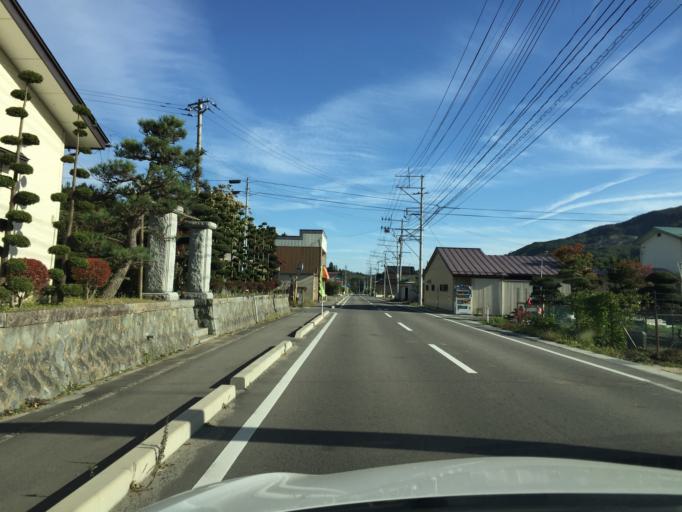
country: JP
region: Fukushima
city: Funehikimachi-funehiki
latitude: 37.3418
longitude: 140.5651
